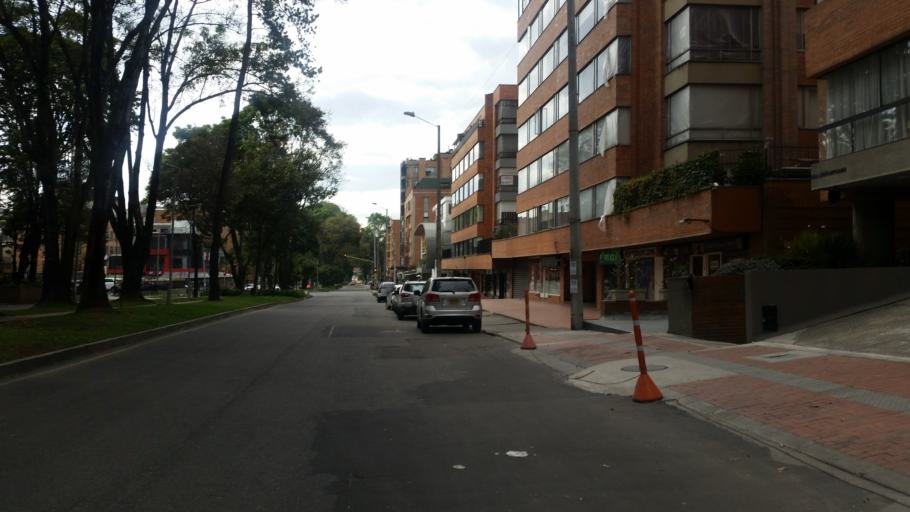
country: CO
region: Bogota D.C.
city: Barrio San Luis
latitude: 4.6779
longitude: -74.0473
